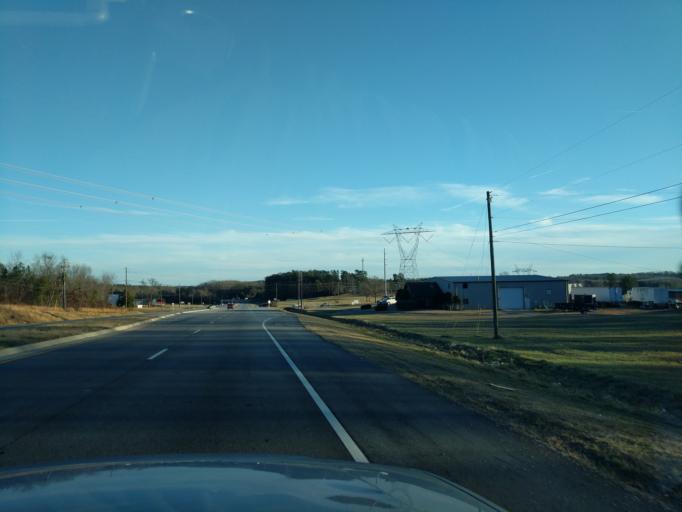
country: US
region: Georgia
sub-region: Stephens County
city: Toccoa
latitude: 34.5431
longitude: -83.2701
